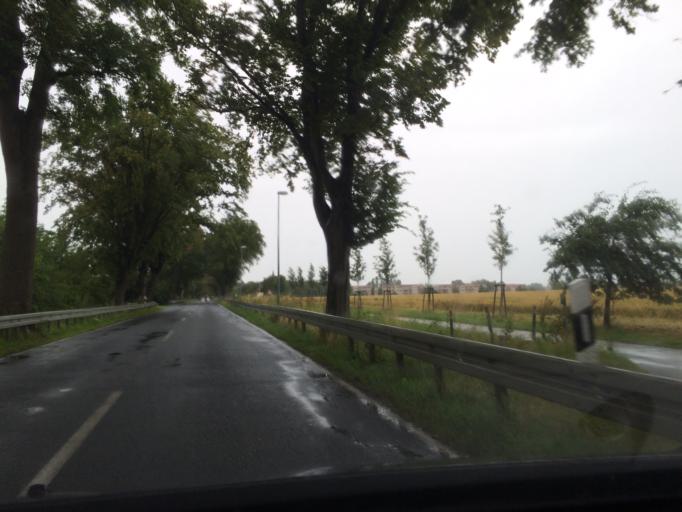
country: DE
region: Mecklenburg-Vorpommern
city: Prohn
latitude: 54.3611
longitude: 13.0328
